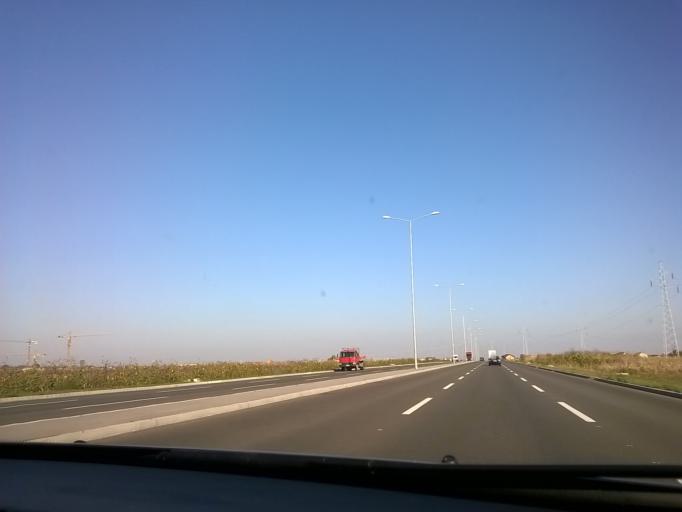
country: RS
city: Ovca
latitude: 44.8783
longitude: 20.5183
